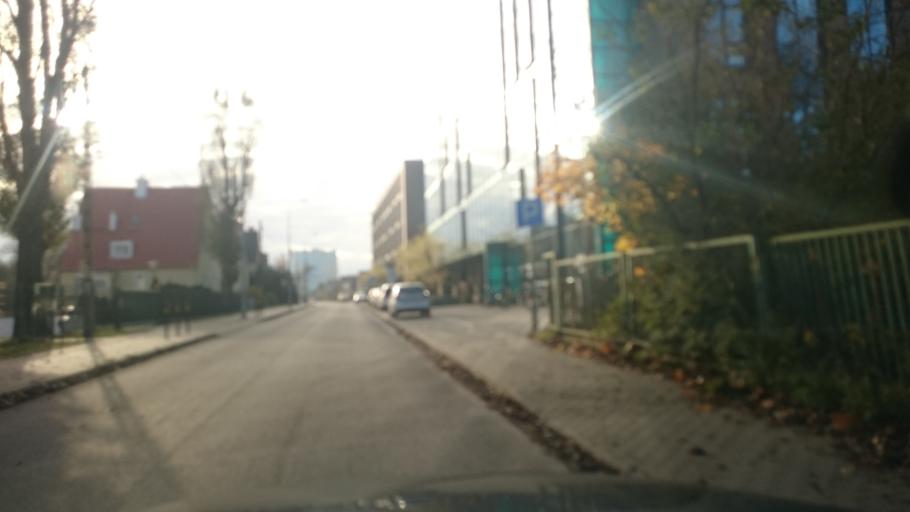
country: PL
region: Pomeranian Voivodeship
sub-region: Sopot
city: Sopot
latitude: 54.4061
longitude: 18.5773
